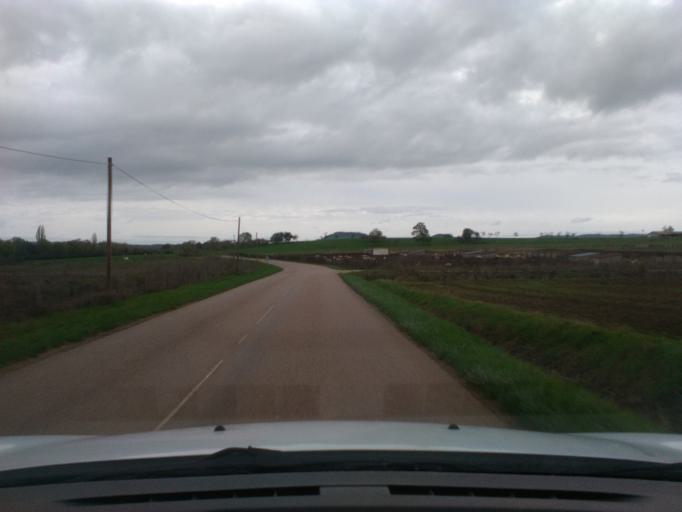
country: FR
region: Lorraine
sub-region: Departement des Vosges
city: Mirecourt
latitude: 48.3481
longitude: 6.0968
